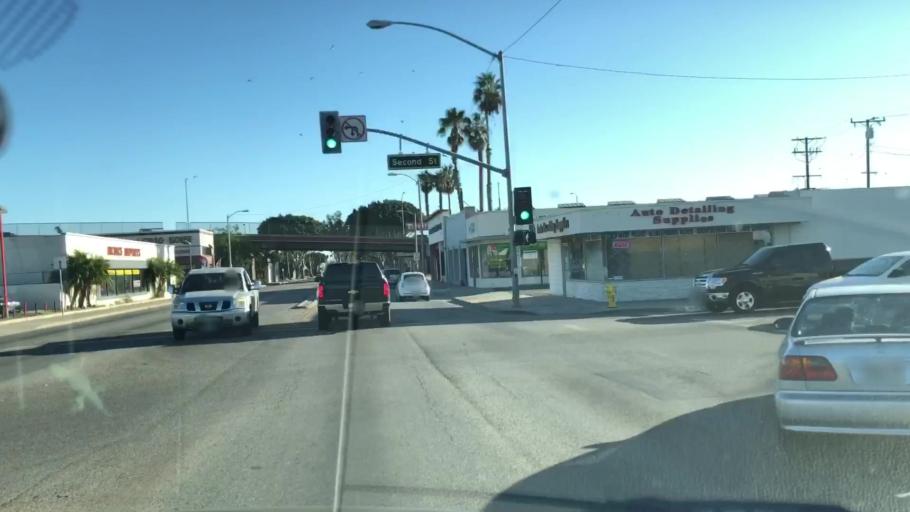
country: US
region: California
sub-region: Ventura County
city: Oxnard
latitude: 34.2017
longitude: -119.1774
